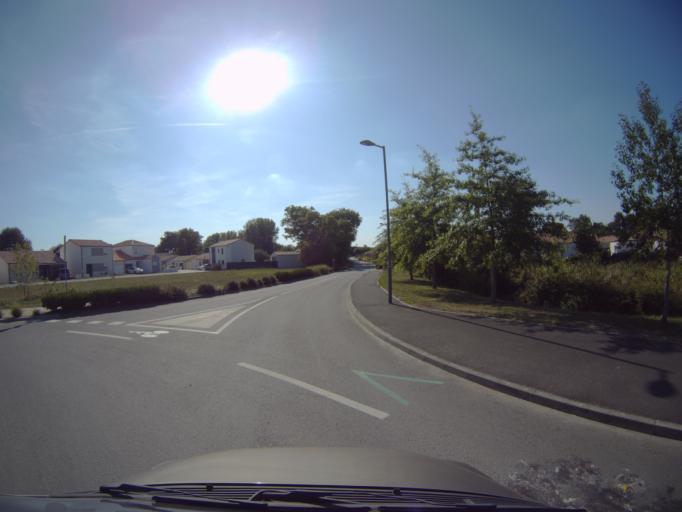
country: FR
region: Pays de la Loire
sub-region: Departement de la Loire-Atlantique
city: Gorges
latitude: 47.0885
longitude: -1.3028
